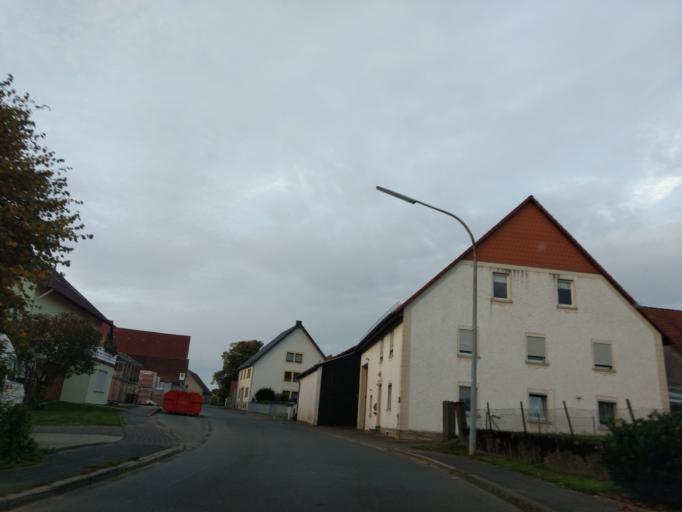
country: DE
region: North Rhine-Westphalia
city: Lichtenau
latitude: 51.6631
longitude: 8.8356
